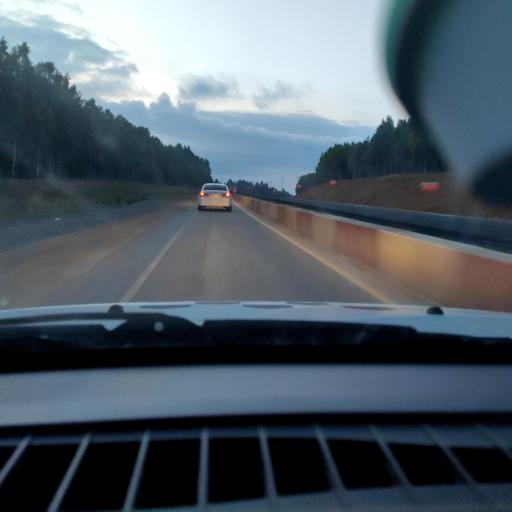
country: RU
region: Sverdlovsk
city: Bisert'
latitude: 56.8297
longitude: 59.1222
